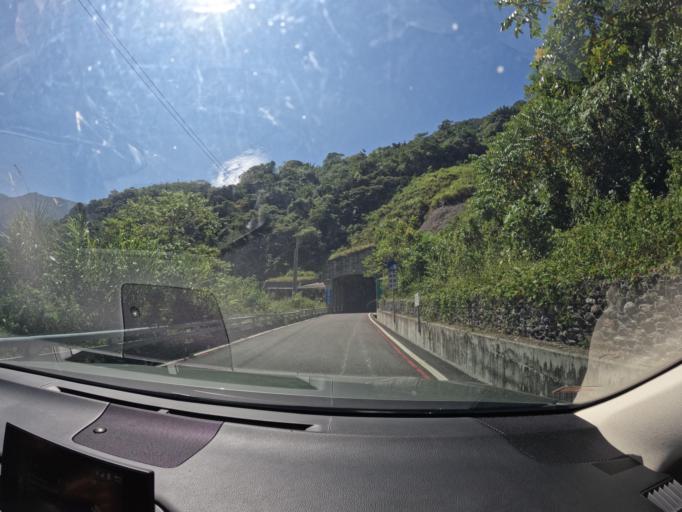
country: TW
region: Taiwan
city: Yujing
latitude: 23.2642
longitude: 120.8394
